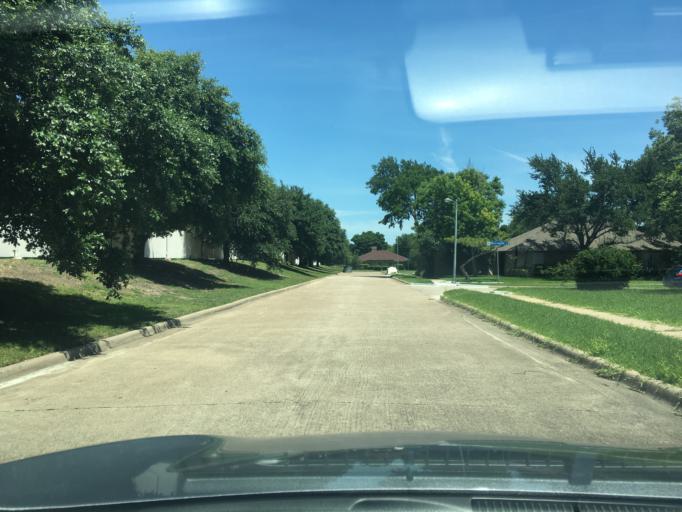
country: US
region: Texas
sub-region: Dallas County
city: Richardson
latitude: 32.9400
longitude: -96.6949
